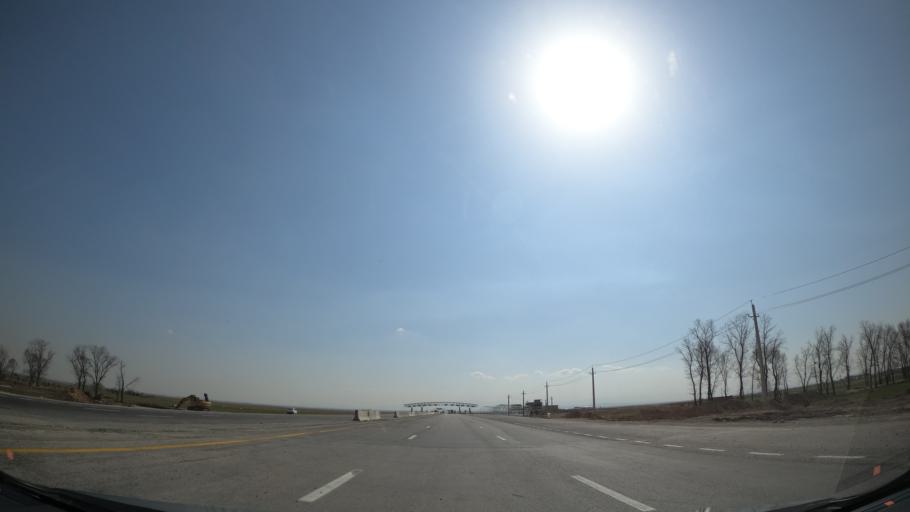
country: IR
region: Qazvin
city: Abyek
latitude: 35.9620
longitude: 50.4634
